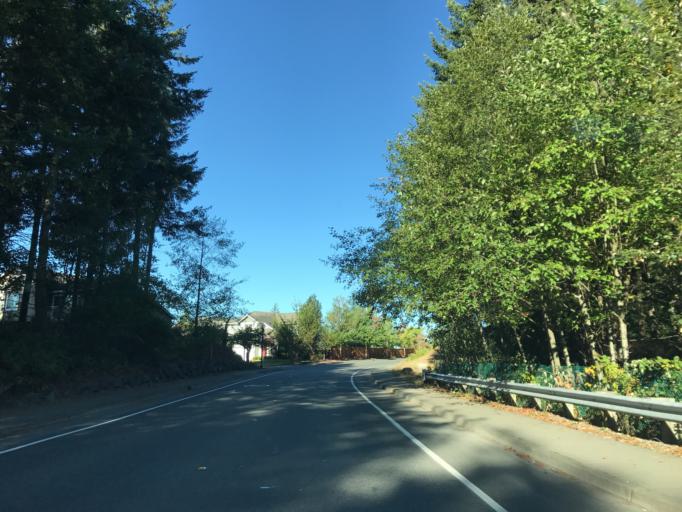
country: US
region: Washington
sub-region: King County
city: Ravensdale
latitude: 47.3520
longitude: -122.0058
